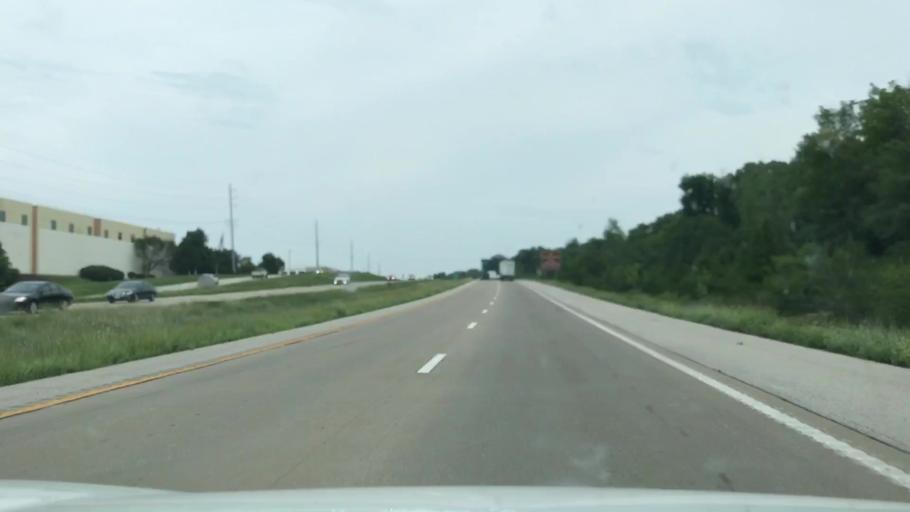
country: US
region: Missouri
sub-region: Saint Charles County
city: Weldon Spring
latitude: 38.7206
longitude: -90.7227
